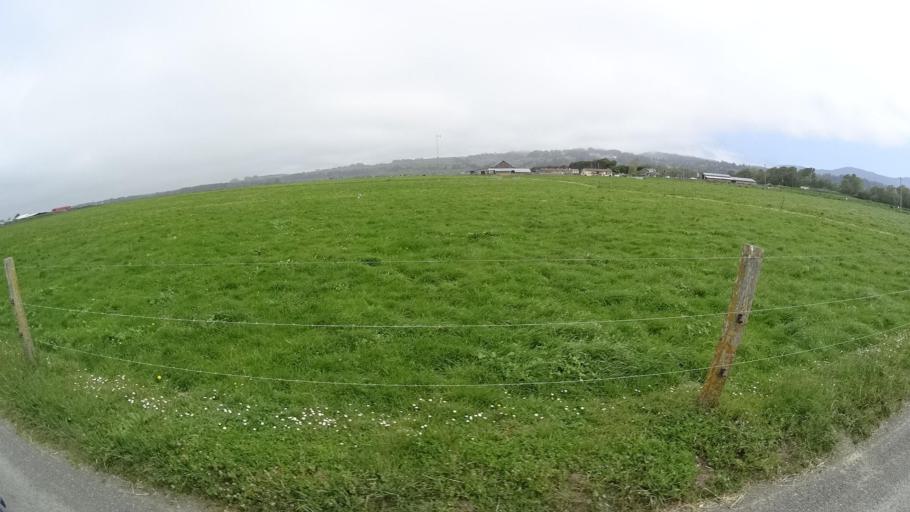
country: US
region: California
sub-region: Humboldt County
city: Fortuna
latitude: 40.5916
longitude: -124.1941
